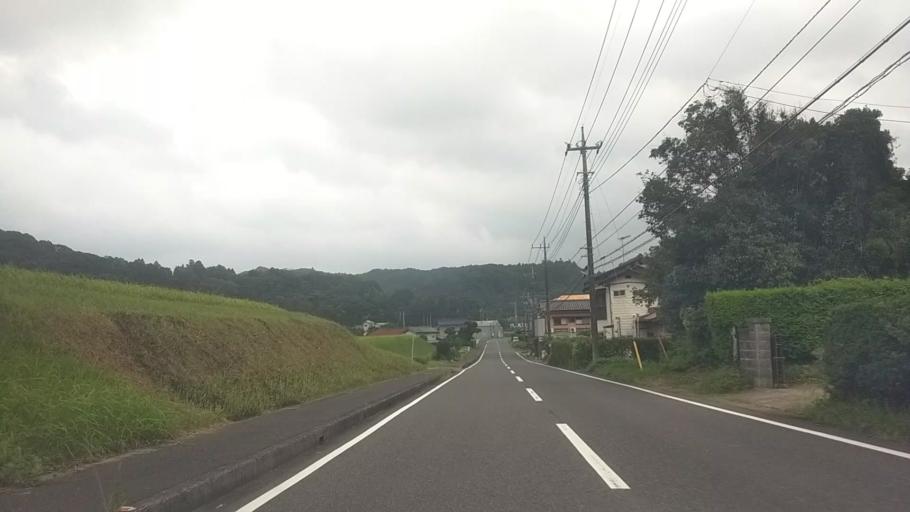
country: JP
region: Chiba
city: Kawaguchi
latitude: 35.2462
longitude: 140.0800
